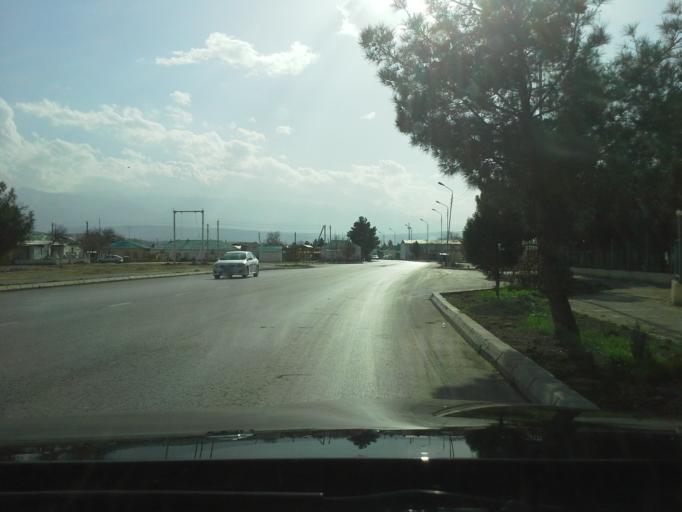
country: TM
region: Ahal
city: Ashgabat
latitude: 37.9903
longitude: 58.2889
